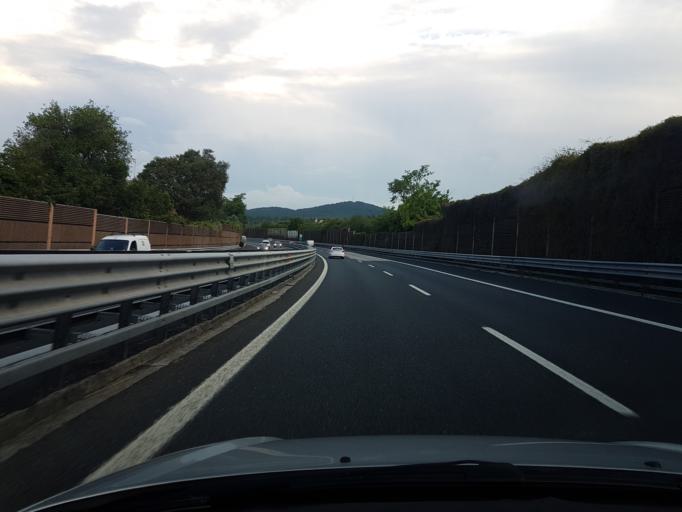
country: IT
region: Friuli Venezia Giulia
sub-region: Provincia di Trieste
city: Sistiana-Visogliano
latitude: 45.7730
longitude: 13.6417
